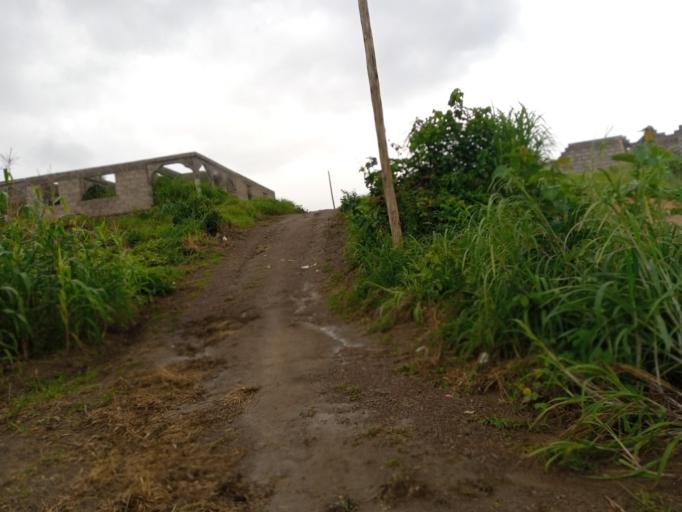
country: SL
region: Eastern Province
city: Kenema
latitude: 7.8587
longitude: -11.1700
